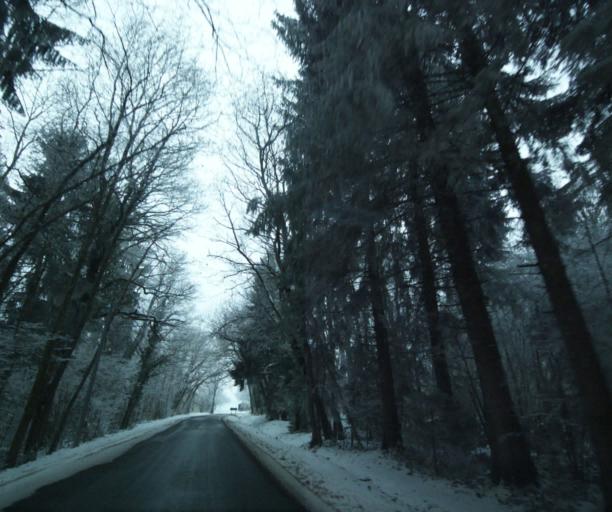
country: FR
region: Rhone-Alpes
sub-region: Departement de la Haute-Savoie
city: Pers-Jussy
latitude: 46.1173
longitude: 6.2308
